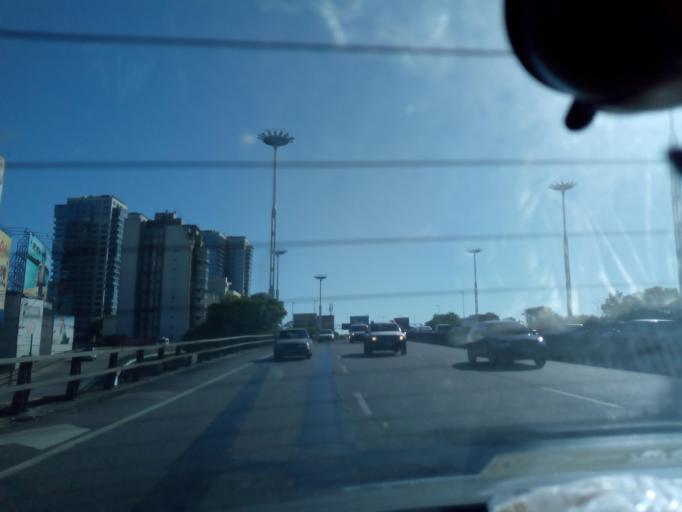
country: AR
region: Buenos Aires
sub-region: Partido de Vicente Lopez
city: Olivos
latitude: -34.5357
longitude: -58.4684
